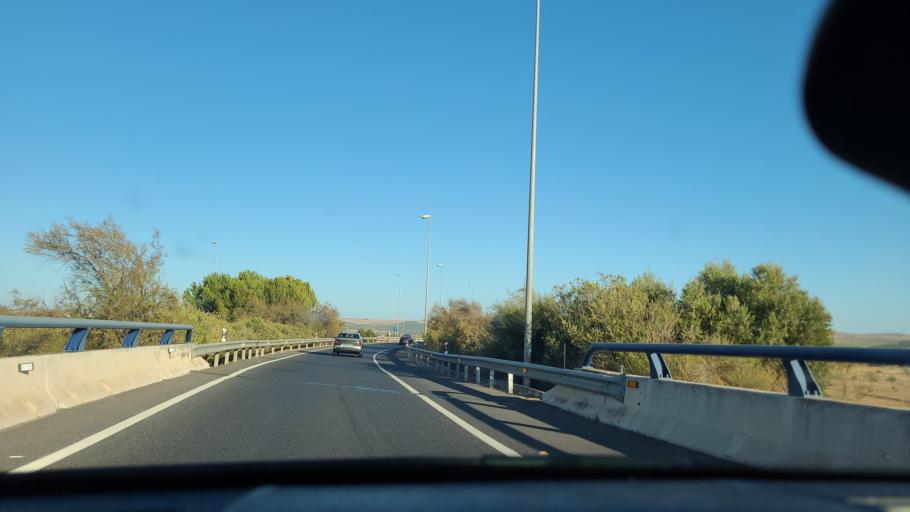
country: ES
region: Andalusia
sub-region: Province of Cordoba
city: Cordoba
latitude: 37.9041
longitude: -4.7522
